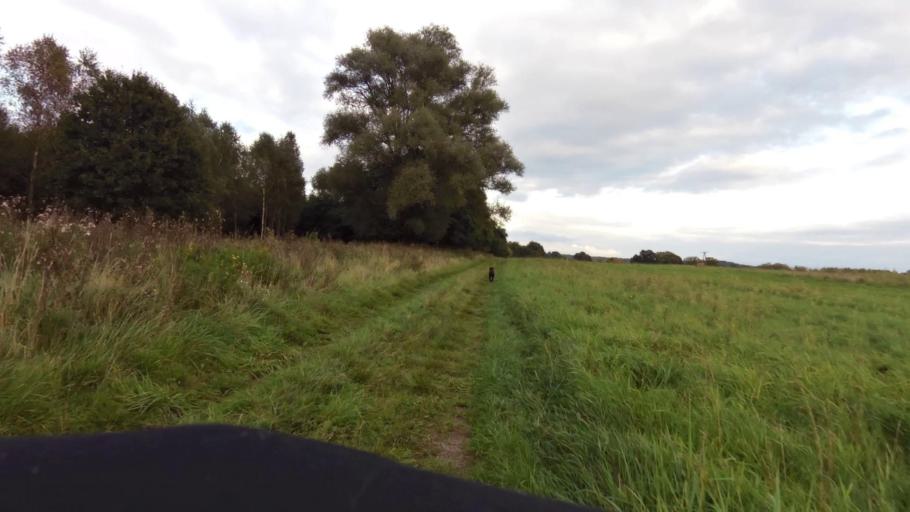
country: PL
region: West Pomeranian Voivodeship
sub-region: Powiat stargardzki
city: Dobrzany
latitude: 53.3823
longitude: 15.4019
